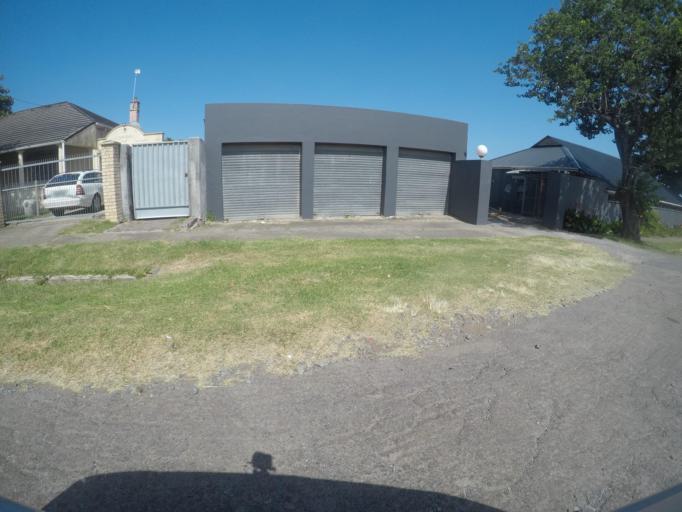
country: ZA
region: Eastern Cape
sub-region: Buffalo City Metropolitan Municipality
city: East London
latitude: -32.9702
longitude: 27.8775
